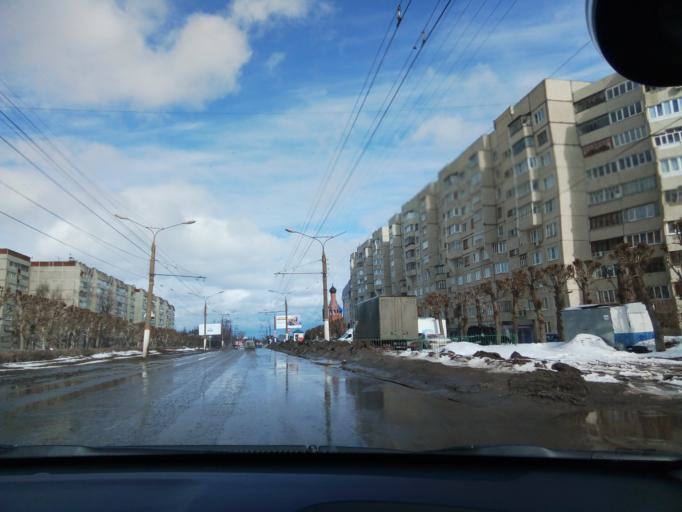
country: RU
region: Chuvashia
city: Novyye Lapsary
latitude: 56.1168
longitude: 47.1920
